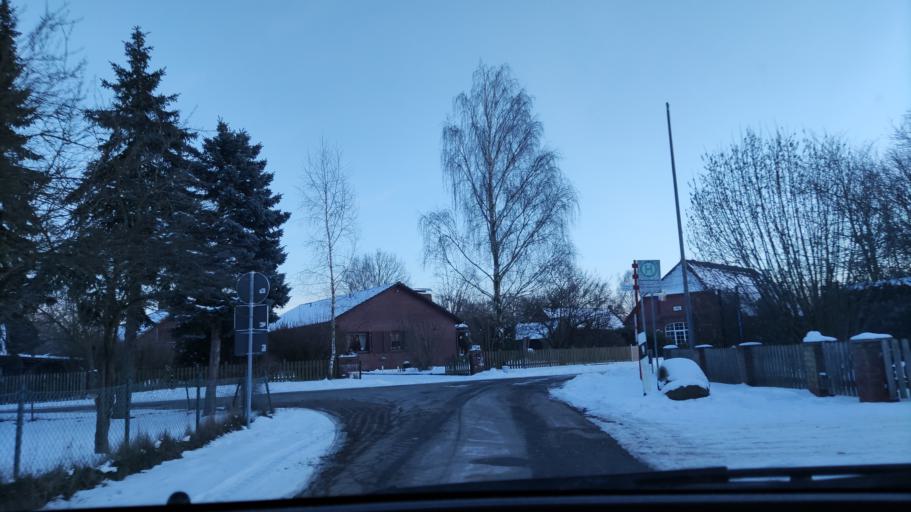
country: DE
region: Lower Saxony
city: Neetze
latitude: 53.2977
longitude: 10.6666
